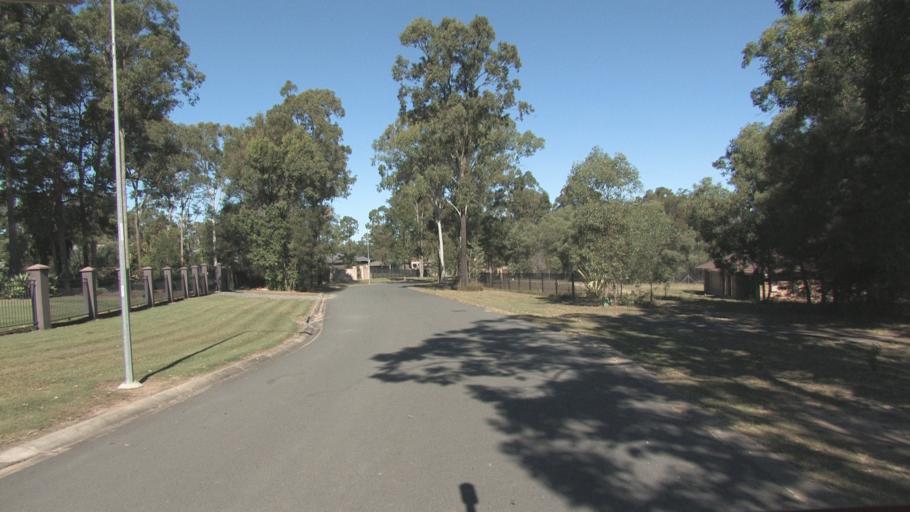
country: AU
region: Queensland
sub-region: Logan
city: Park Ridge South
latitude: -27.7118
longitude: 153.0452
